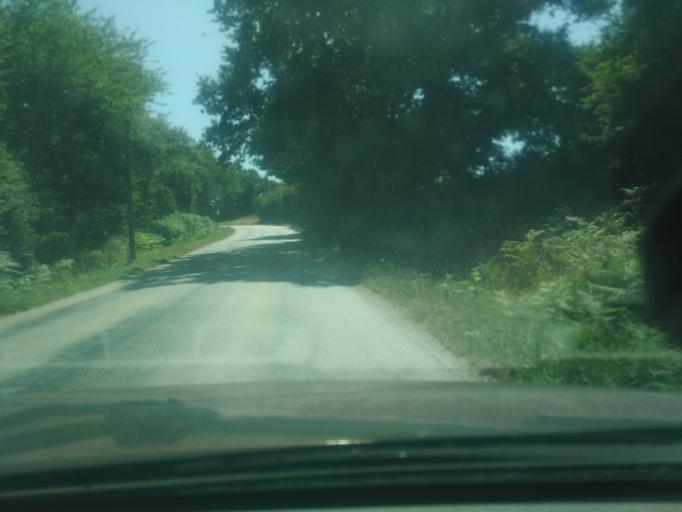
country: FR
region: Pays de la Loire
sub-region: Departement de la Vendee
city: Dompierre-sur-Yon
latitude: 46.7181
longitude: -1.3958
